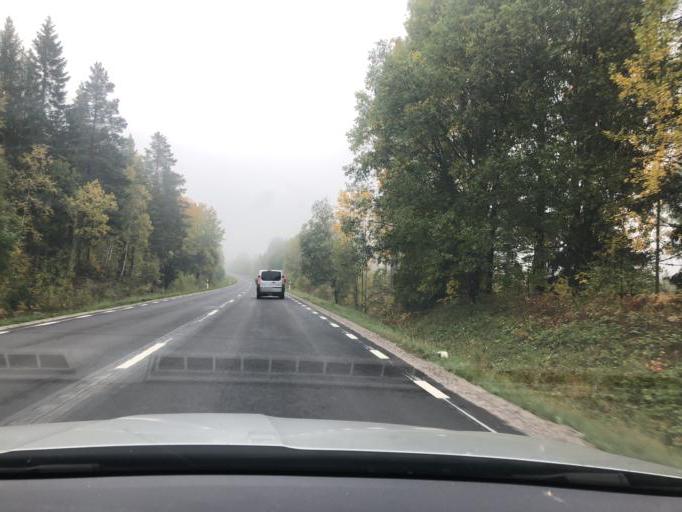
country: SE
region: Uppsala
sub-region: Tierps Kommun
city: Tierp
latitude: 60.2824
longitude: 17.5906
